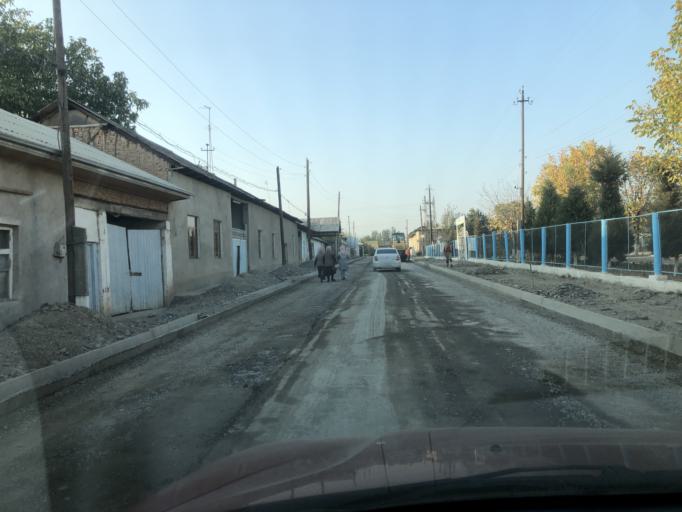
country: UZ
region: Namangan
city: Uychi
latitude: 41.0821
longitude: 71.9994
